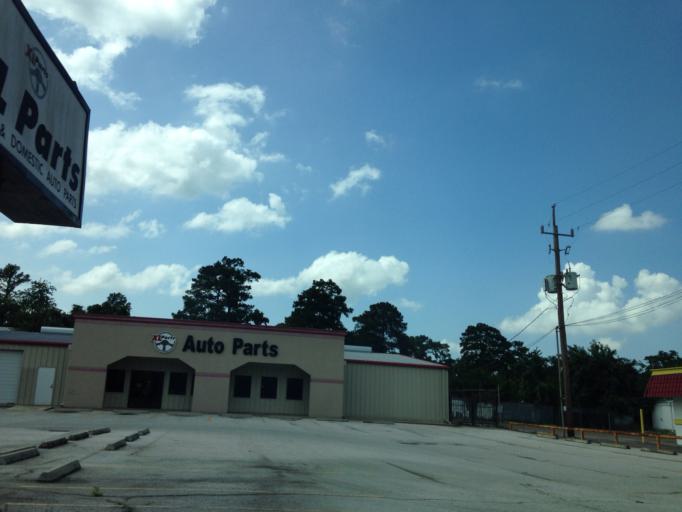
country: US
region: Texas
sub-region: Harris County
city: Spring
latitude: 30.0157
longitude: -95.4480
